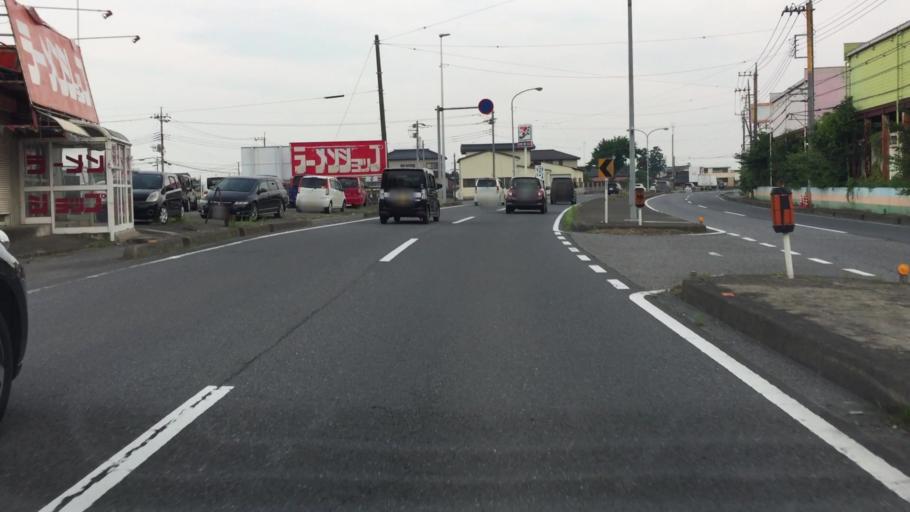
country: JP
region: Tochigi
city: Tochigi
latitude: 36.3605
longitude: 139.7169
